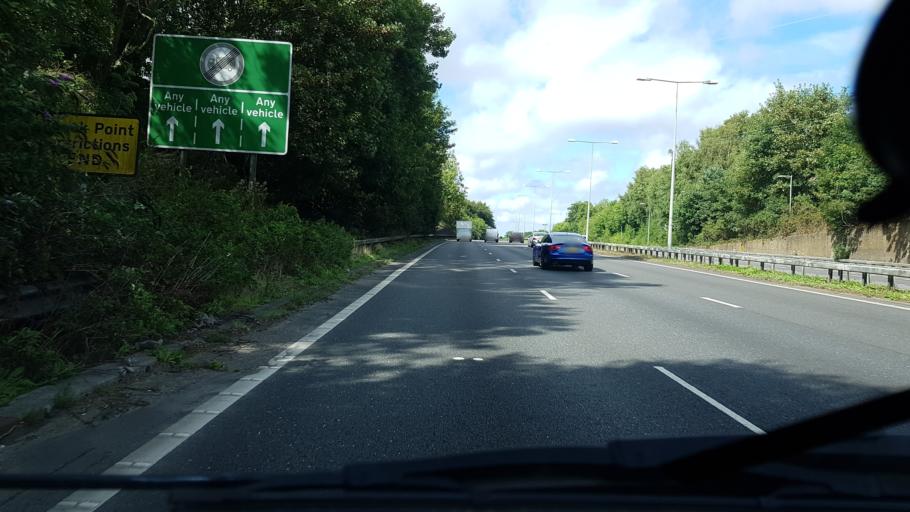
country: GB
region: England
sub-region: West Sussex
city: Broadfield
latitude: 51.0532
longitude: -0.2021
